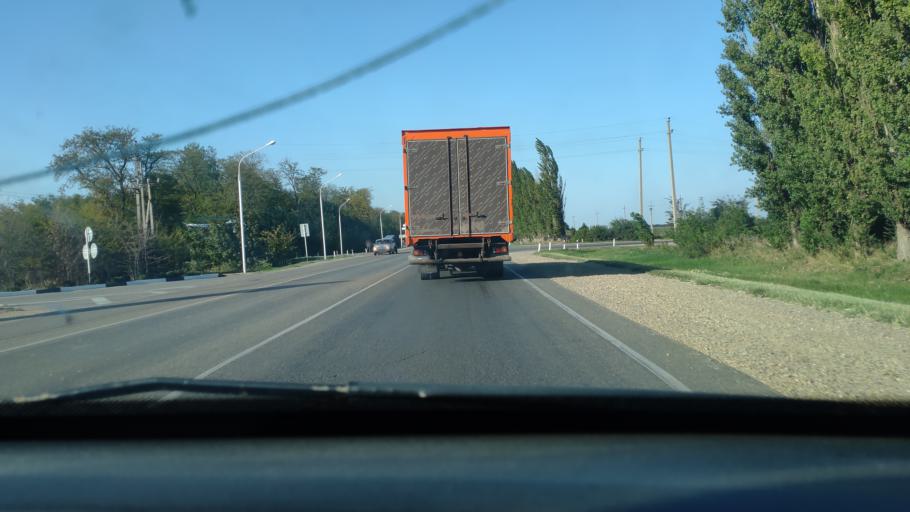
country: RU
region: Krasnodarskiy
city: Novotitarovskaya
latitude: 45.2602
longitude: 38.9991
